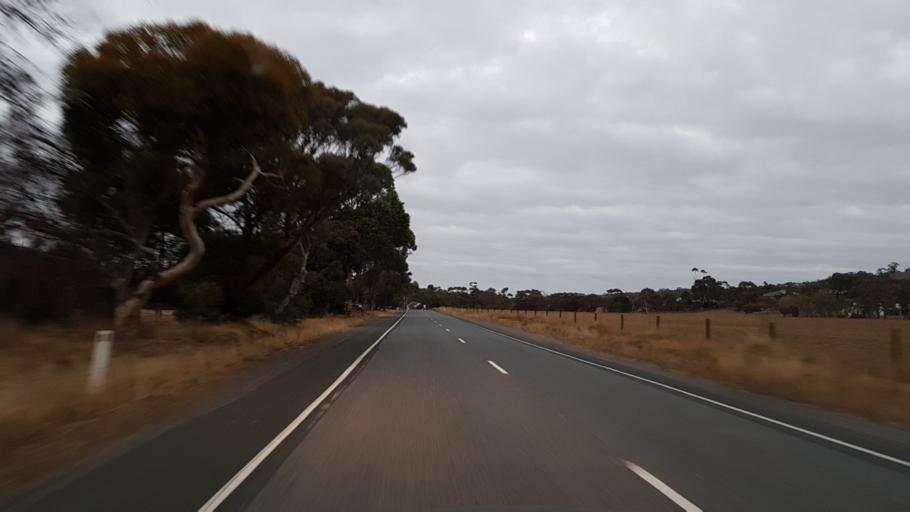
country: AU
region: South Australia
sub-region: Mount Barker
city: Callington
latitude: -35.0638
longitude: 139.0122
